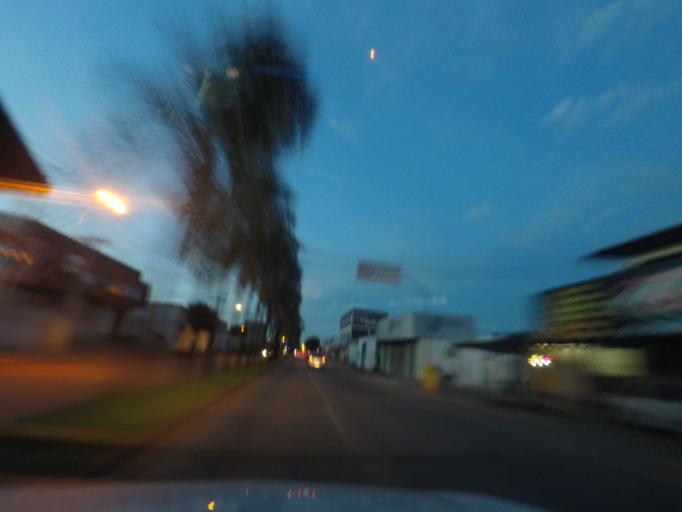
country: BR
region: Goias
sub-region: Goiania
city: Goiania
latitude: -16.7068
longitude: -49.3149
